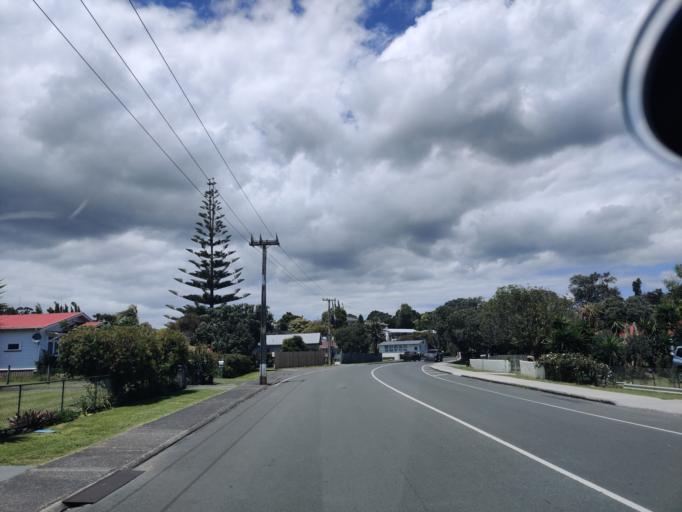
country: NZ
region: Northland
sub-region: Far North District
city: Kaitaia
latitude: -35.1124
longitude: 173.2587
